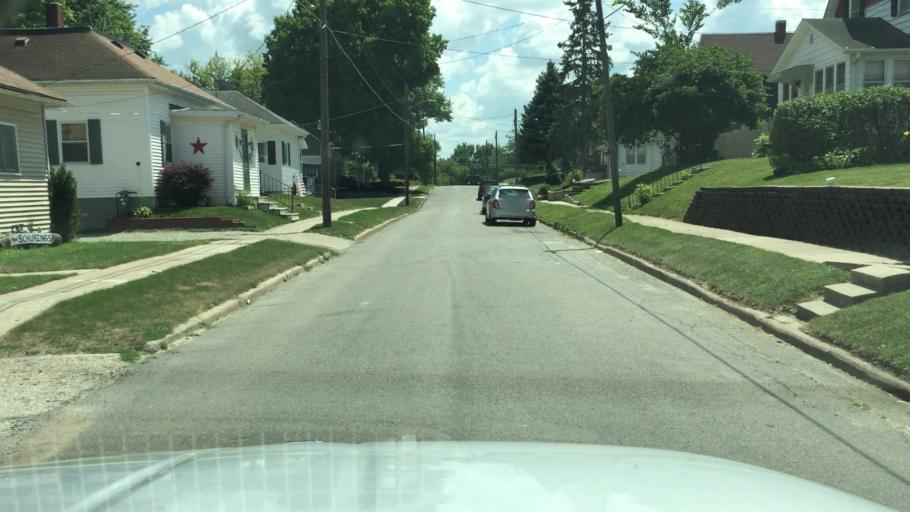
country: US
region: Iowa
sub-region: Jasper County
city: Newton
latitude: 41.6942
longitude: -93.0549
